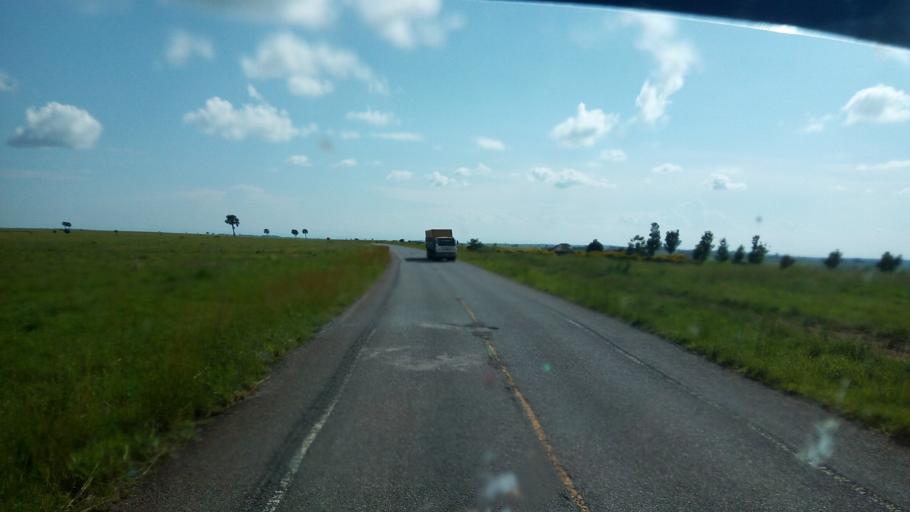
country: UG
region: Northern Region
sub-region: Nwoya District
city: Nwoya
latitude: 2.5621
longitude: 31.6580
